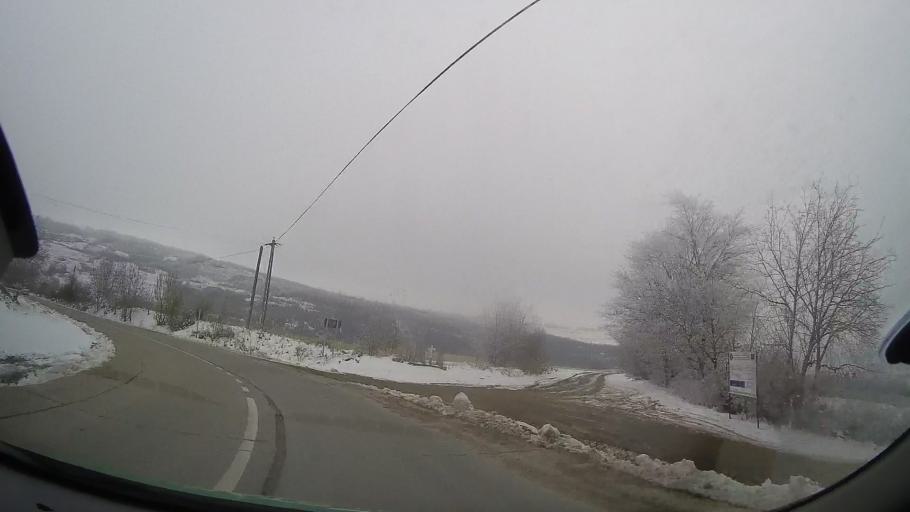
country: RO
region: Vrancea
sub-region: Comuna Boghesti
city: Boghesti
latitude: 46.1953
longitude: 27.4412
